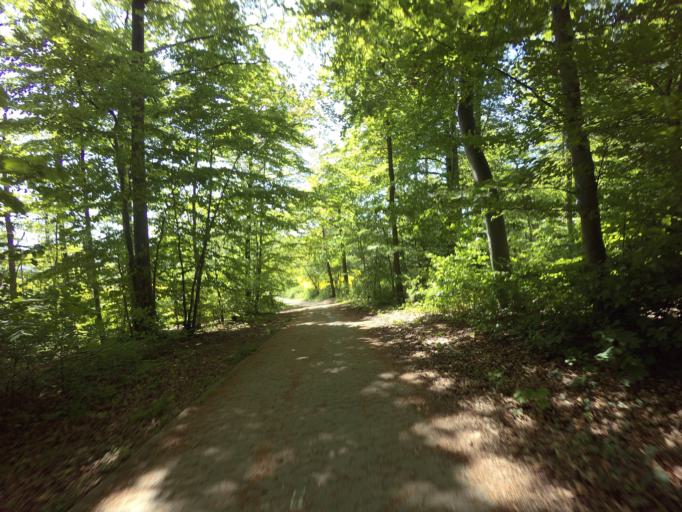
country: DE
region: Lower Saxony
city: Hildesheim
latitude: 52.1347
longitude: 9.9932
